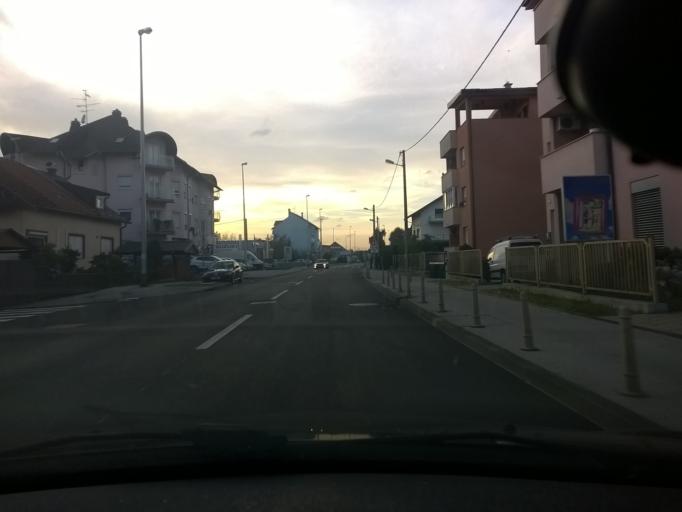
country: HR
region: Grad Zagreb
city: Stenjevec
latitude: 45.8115
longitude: 15.8714
